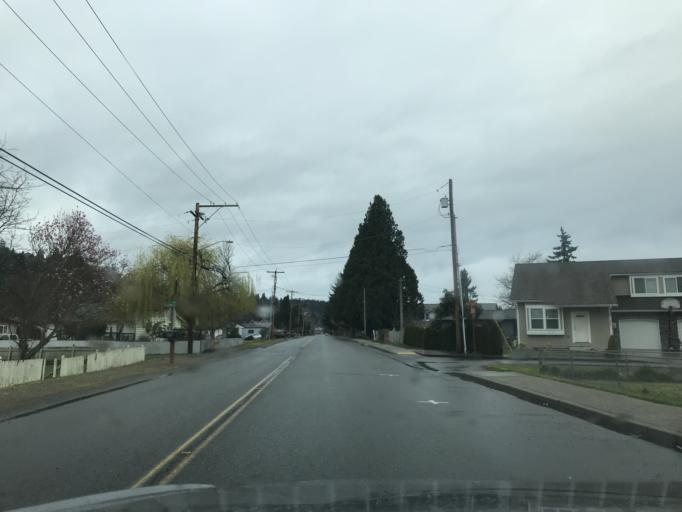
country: US
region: Washington
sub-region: King County
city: Algona
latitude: 47.2812
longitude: -122.2523
